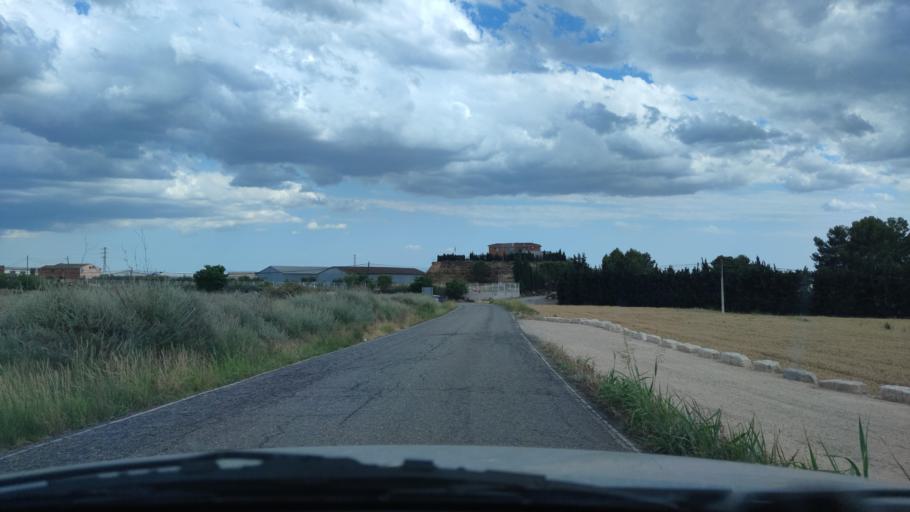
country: ES
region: Catalonia
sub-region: Provincia de Lleida
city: Lleida
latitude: 41.6008
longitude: 0.5894
